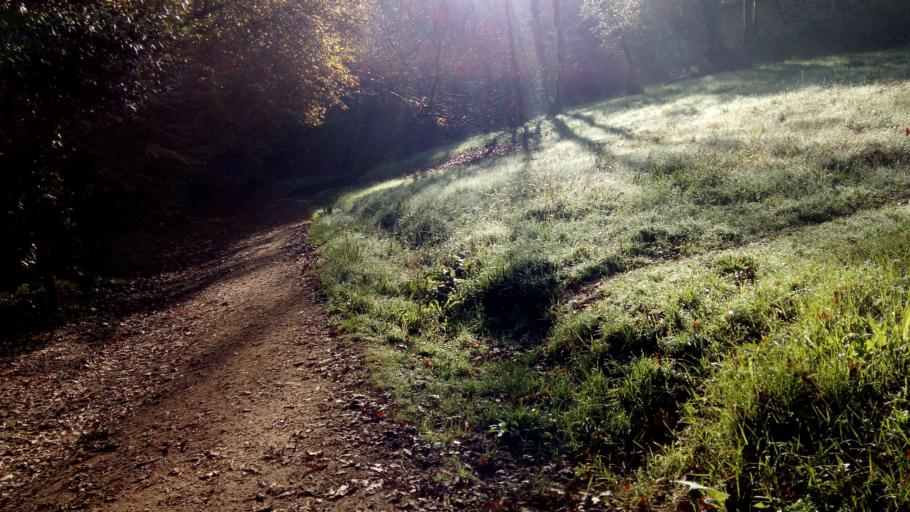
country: ES
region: Galicia
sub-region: Provincia de Pontevedra
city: Meis
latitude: 42.4894
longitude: -8.7526
